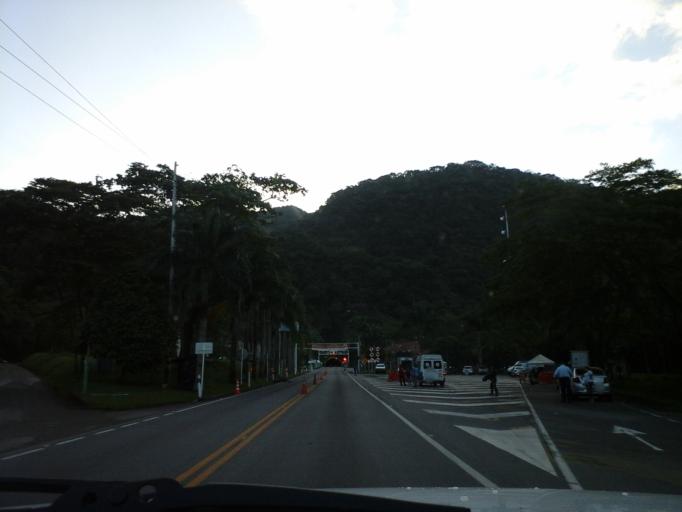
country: CO
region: Meta
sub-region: Villavicencio
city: Villavicencio
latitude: 4.1421
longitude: -73.6607
